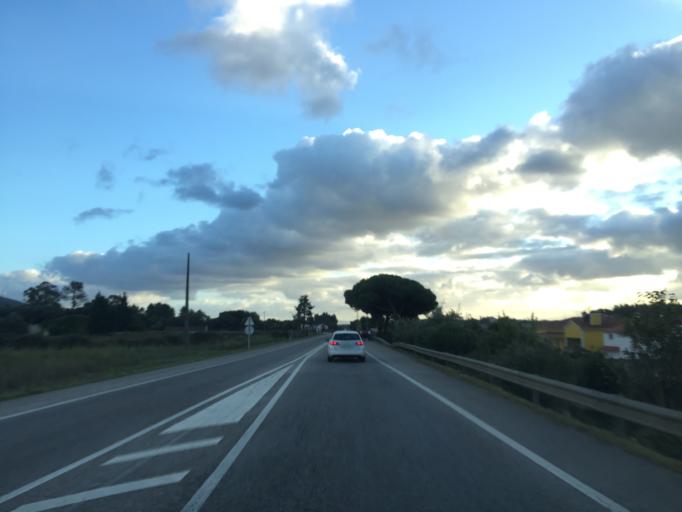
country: PT
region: Leiria
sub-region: Alcobaca
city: Benedita
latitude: 39.4456
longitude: -8.9518
